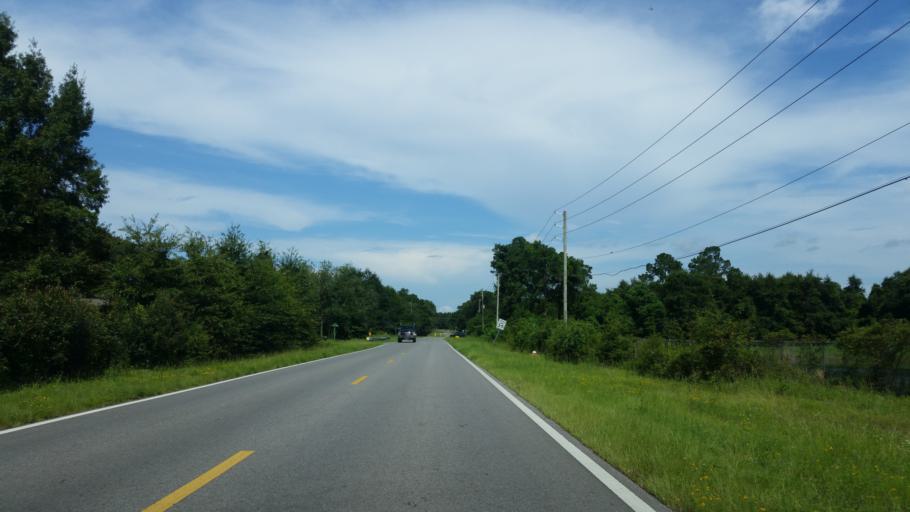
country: US
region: Florida
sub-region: Santa Rosa County
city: Pace
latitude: 30.5894
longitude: -87.1492
